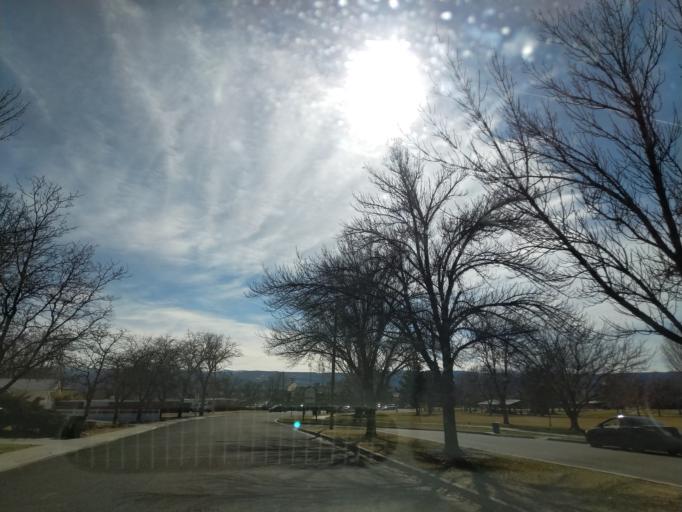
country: US
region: Colorado
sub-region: Mesa County
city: Grand Junction
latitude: 39.0809
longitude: -108.5668
